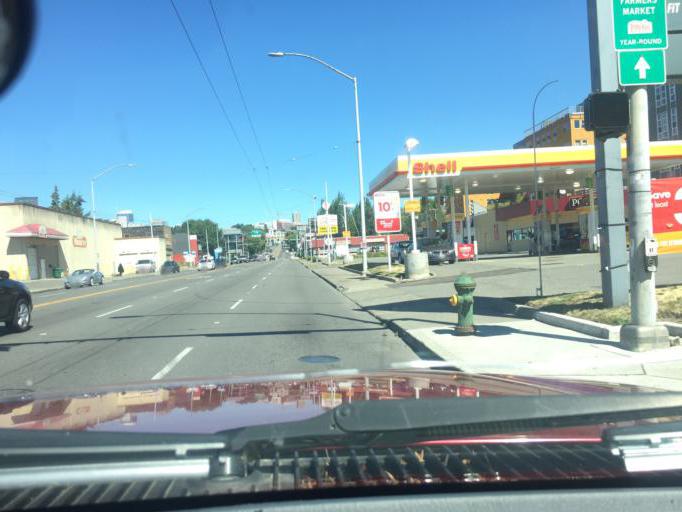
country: US
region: Washington
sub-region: King County
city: Seattle
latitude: 47.5941
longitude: -122.3101
